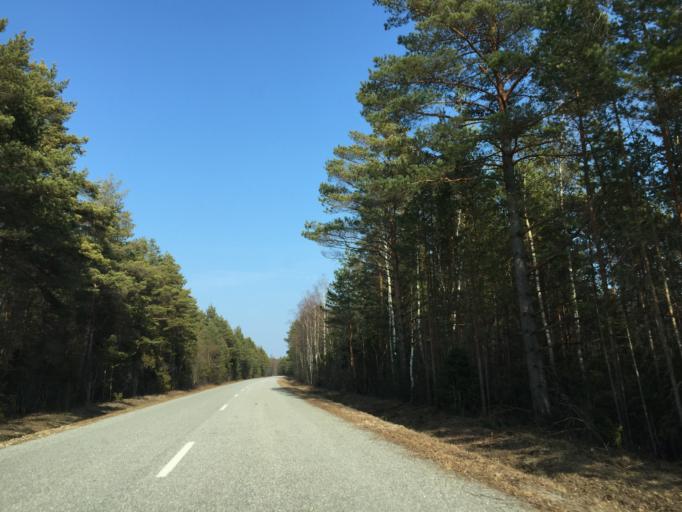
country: EE
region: Saare
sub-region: Orissaare vald
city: Orissaare
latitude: 58.5709
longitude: 23.3621
